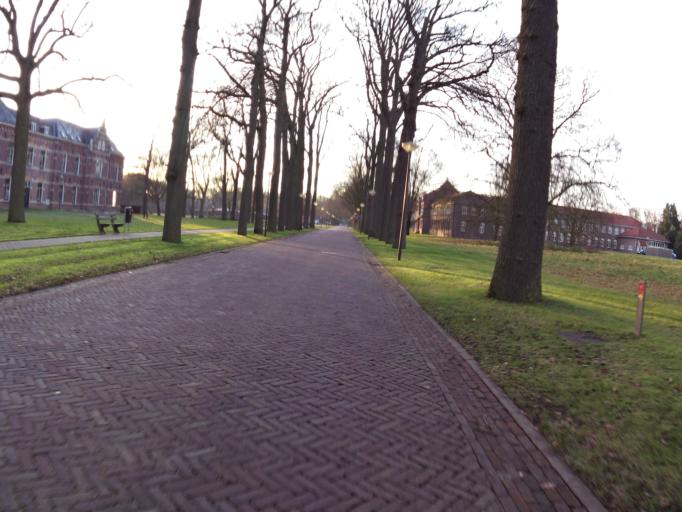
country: NL
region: North Brabant
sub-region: Gemeente Vught
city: Vught
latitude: 51.6412
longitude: 5.3051
